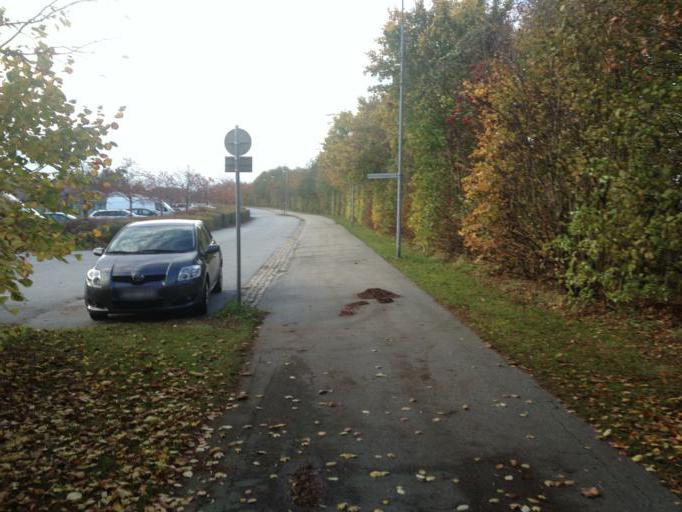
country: SE
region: Skane
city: Bjarred
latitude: 55.7253
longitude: 13.0344
